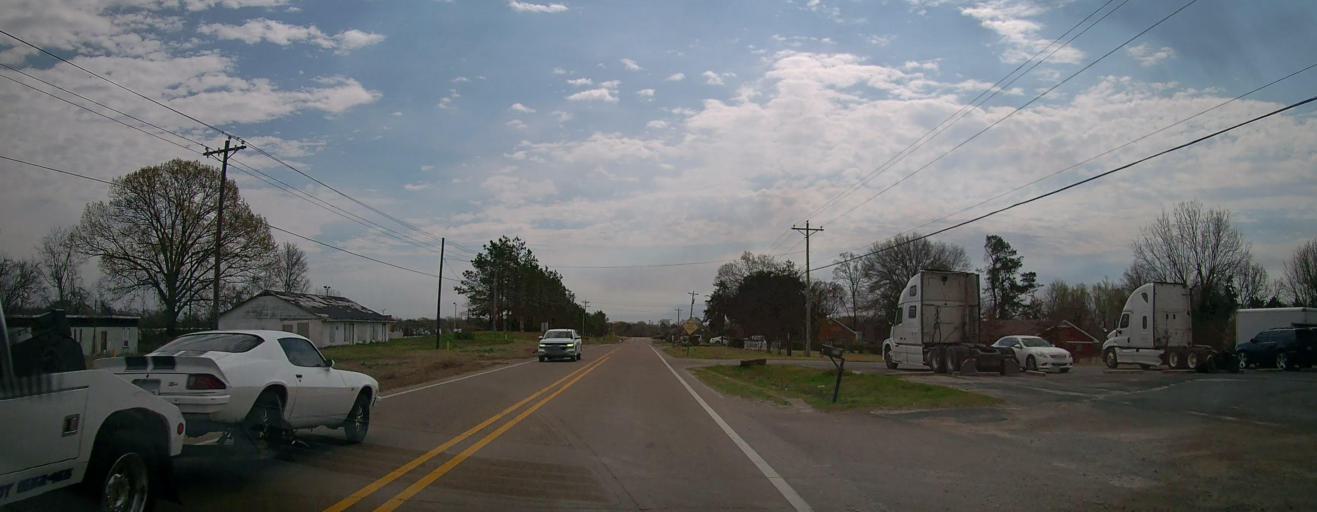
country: US
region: Mississippi
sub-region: De Soto County
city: Olive Branch
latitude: 34.9800
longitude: -89.8544
